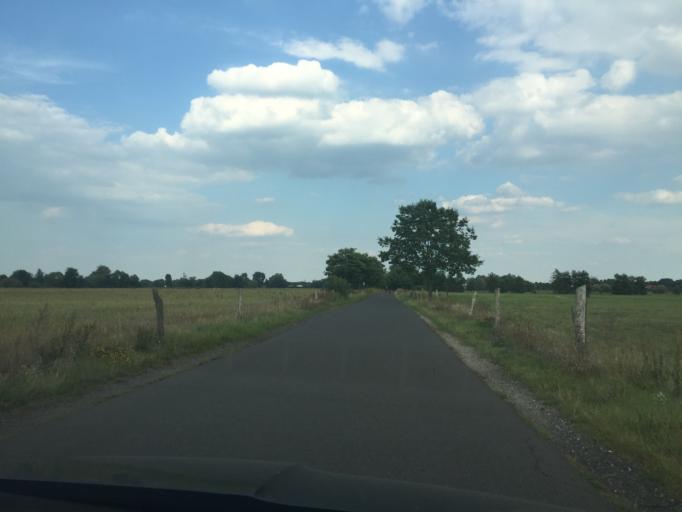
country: DE
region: Brandenburg
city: Spreenhagen
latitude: 52.3552
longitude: 13.8188
